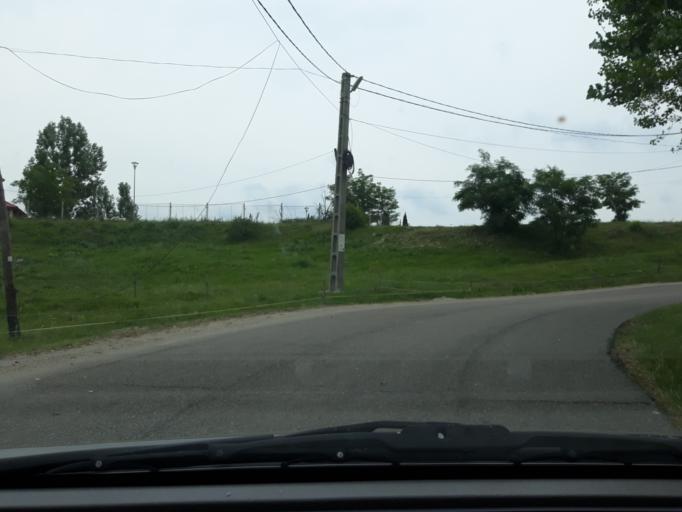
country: RO
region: Salaj
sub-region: Comuna Criseni
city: Criseni
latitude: 47.2434
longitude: 23.0708
